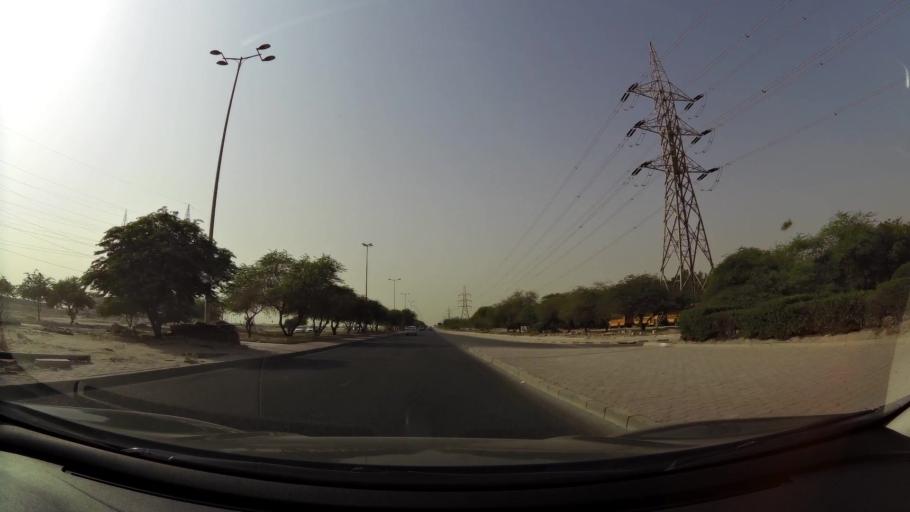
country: KW
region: Al Asimah
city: Ar Rabiyah
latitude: 29.2869
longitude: 47.8468
